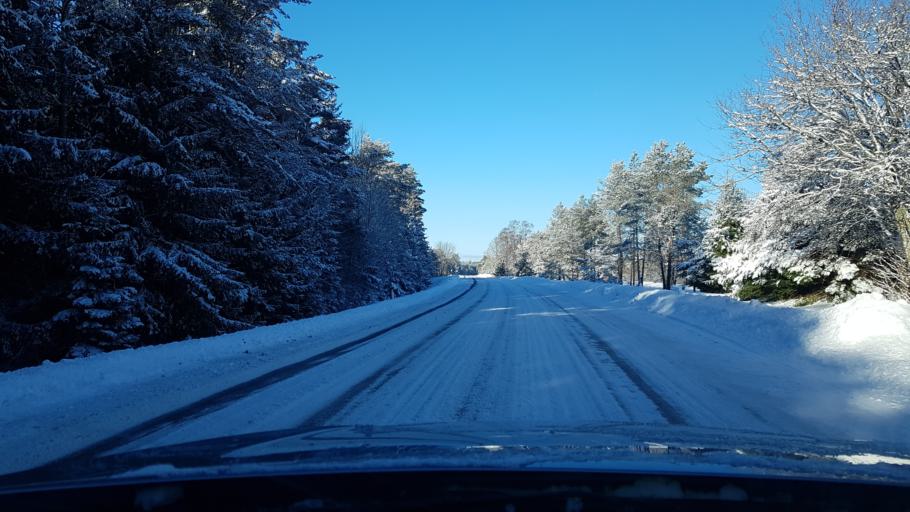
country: EE
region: Hiiumaa
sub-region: Kaerdla linn
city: Kardla
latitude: 58.9411
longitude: 22.7762
